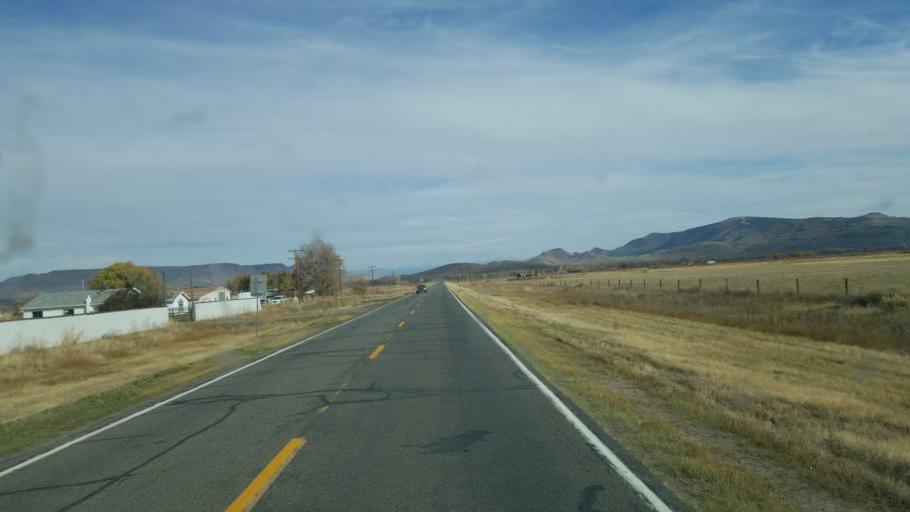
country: US
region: Colorado
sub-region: Conejos County
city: Conejos
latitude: 37.1737
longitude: -105.9248
